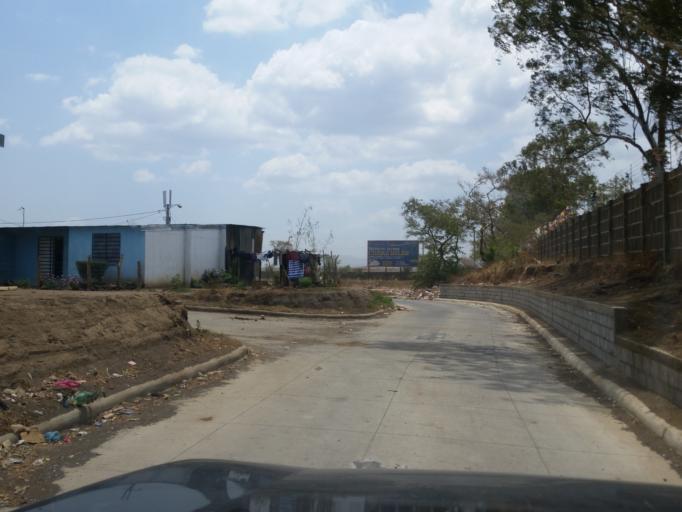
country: NI
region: Managua
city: Managua
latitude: 12.1272
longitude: -86.1595
